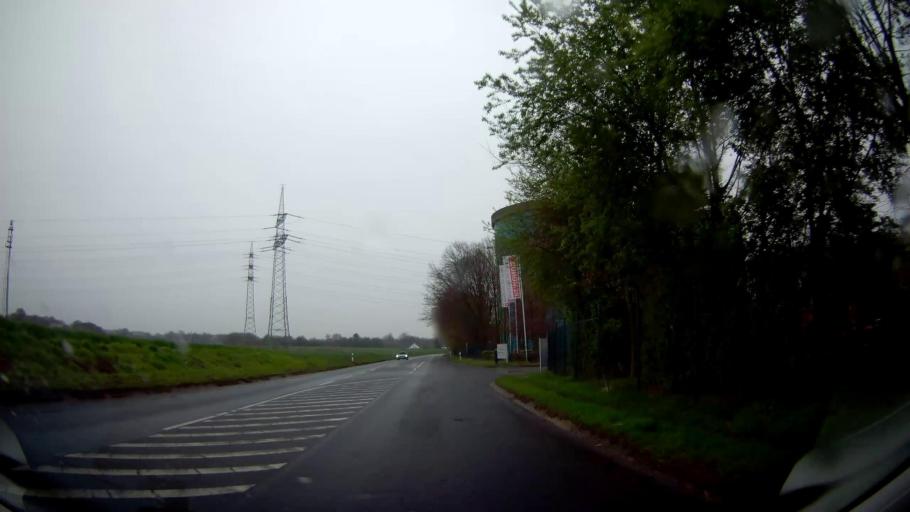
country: DE
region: North Rhine-Westphalia
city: Castrop-Rauxel
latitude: 51.5243
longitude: 7.3037
